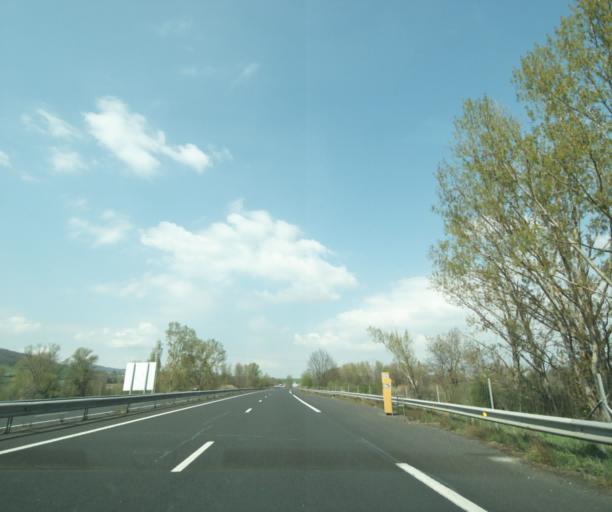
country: FR
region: Auvergne
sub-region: Departement de la Haute-Loire
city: Lempdes-sur-Allagnon
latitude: 45.3907
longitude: 3.2743
